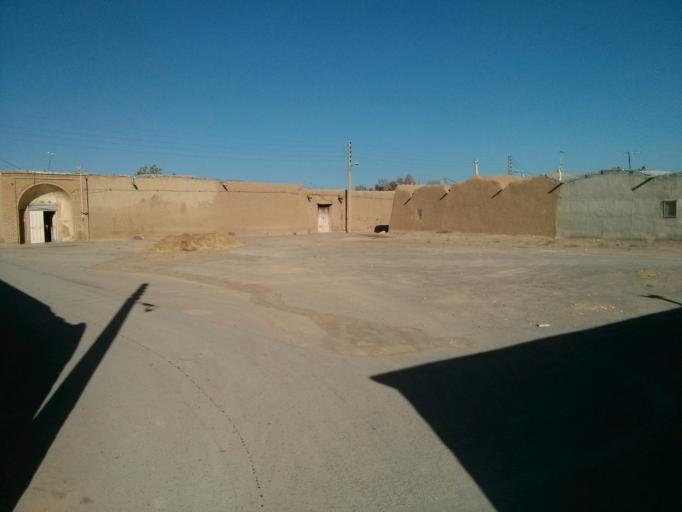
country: IR
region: Isfahan
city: Na'in
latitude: 32.7343
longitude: 52.6784
